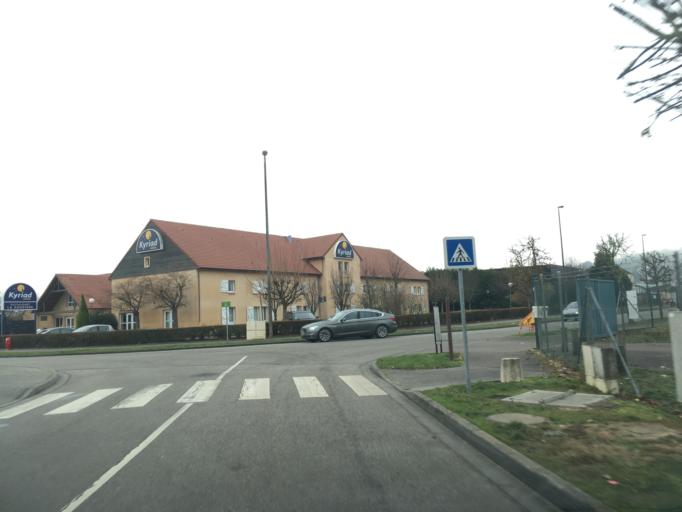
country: FR
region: Haute-Normandie
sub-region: Departement de l'Eure
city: Saint-Marcel
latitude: 49.1052
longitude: 1.4508
